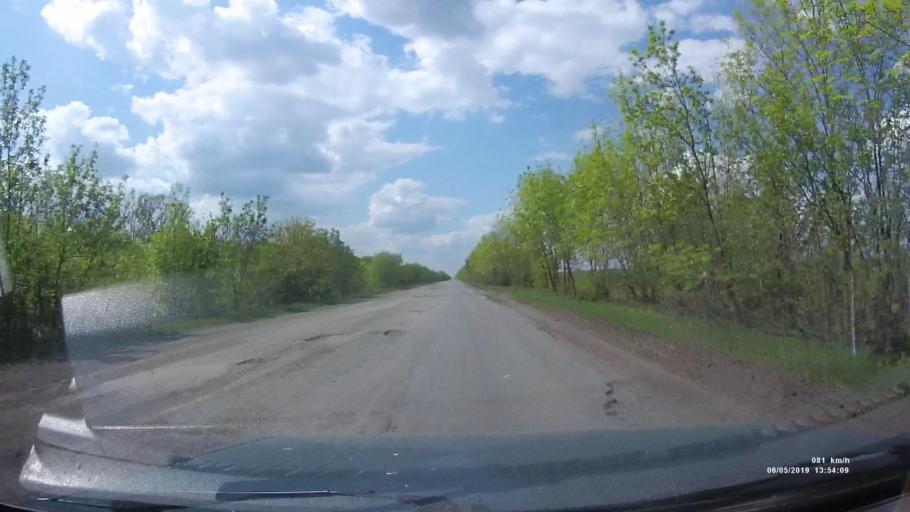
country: RU
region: Rostov
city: Melikhovskaya
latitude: 47.6728
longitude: 40.4513
